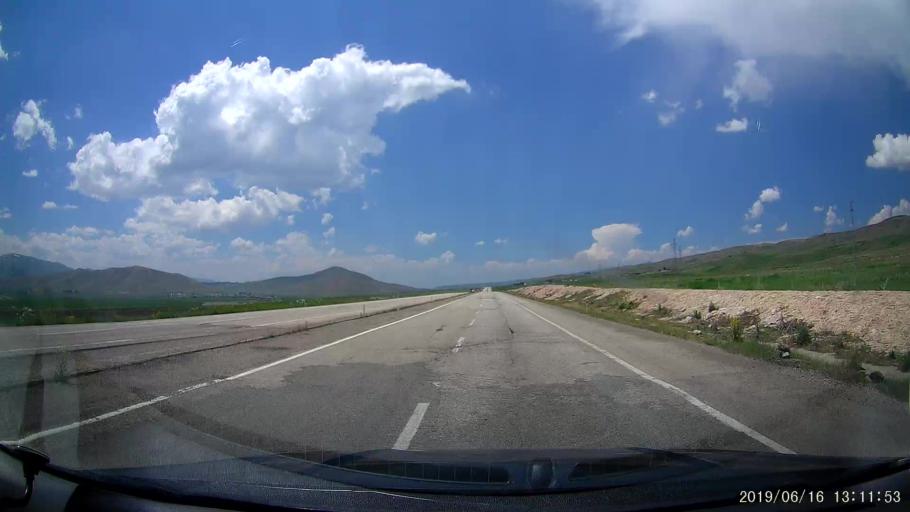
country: TR
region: Agri
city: Diyadin
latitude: 39.5949
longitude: 43.5944
